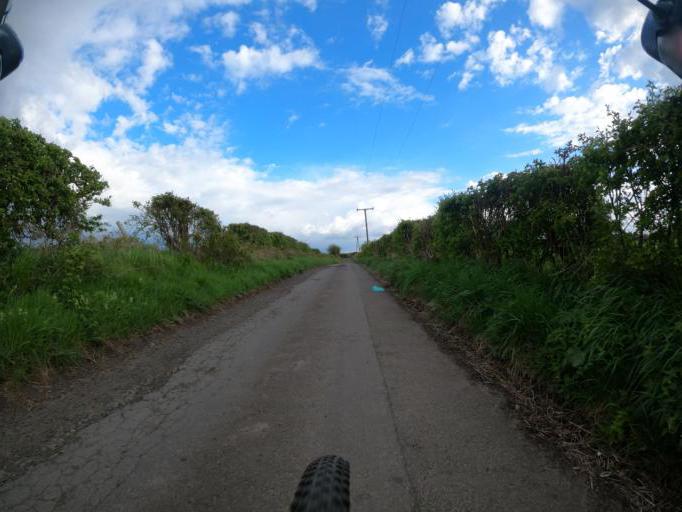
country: GB
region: Scotland
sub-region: Edinburgh
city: Ratho
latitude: 55.9577
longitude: -3.3382
